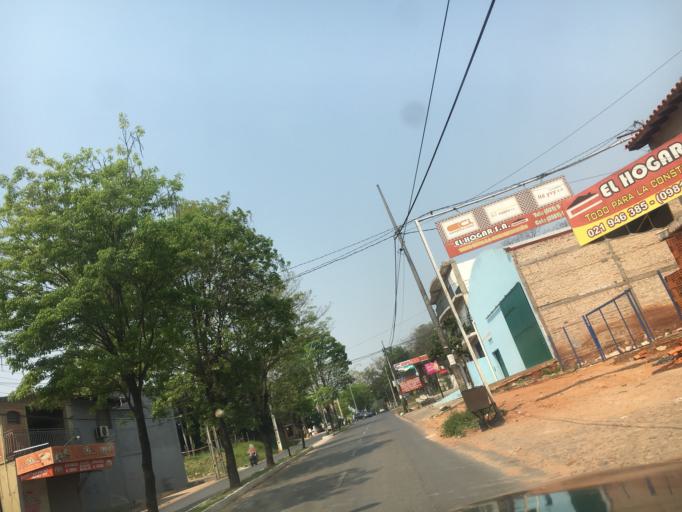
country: PY
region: Central
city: Villa Elisa
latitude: -25.3658
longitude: -57.5889
